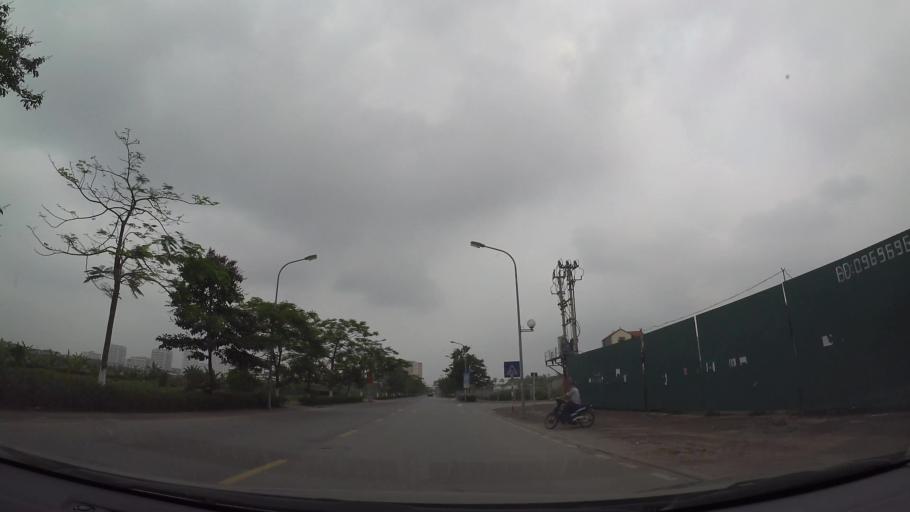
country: VN
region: Ha Noi
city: Trau Quy
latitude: 21.0525
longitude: 105.9205
